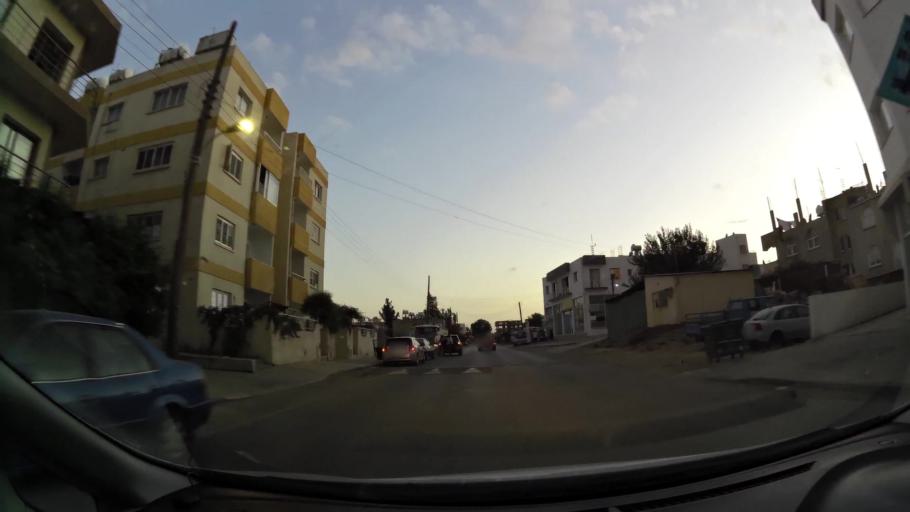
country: CY
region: Lefkosia
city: Nicosia
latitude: 35.1986
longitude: 33.3746
